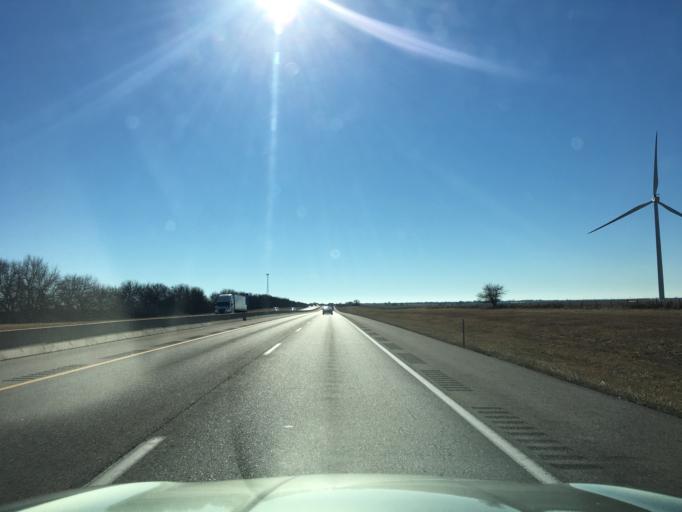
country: US
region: Kansas
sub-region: Sumner County
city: Wellington
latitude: 37.1269
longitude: -97.3390
